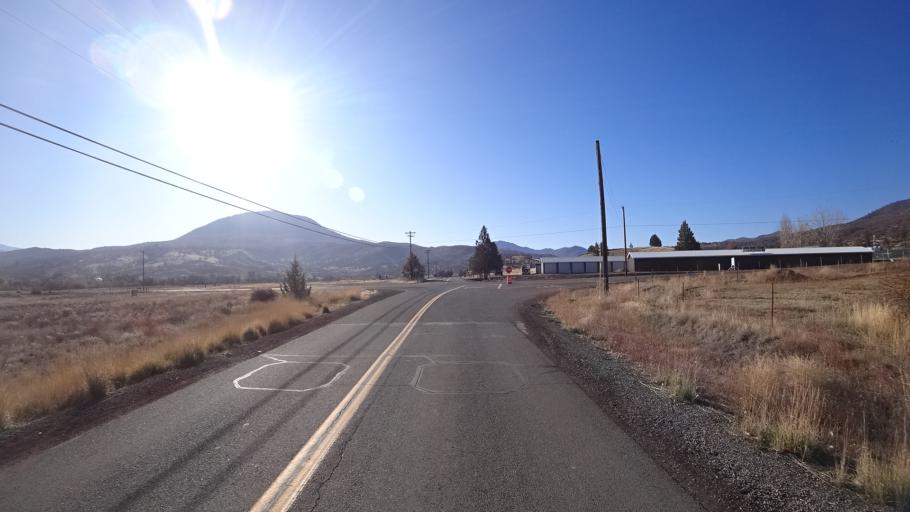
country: US
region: California
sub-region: Siskiyou County
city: Montague
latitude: 41.8986
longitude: -122.5515
